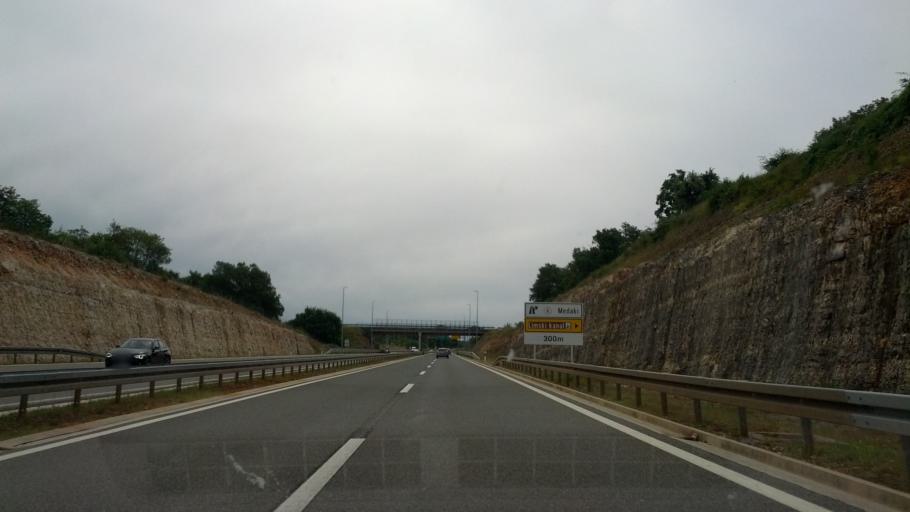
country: HR
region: Istarska
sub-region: Grad Rovinj
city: Rovinj
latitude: 45.1527
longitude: 13.7370
